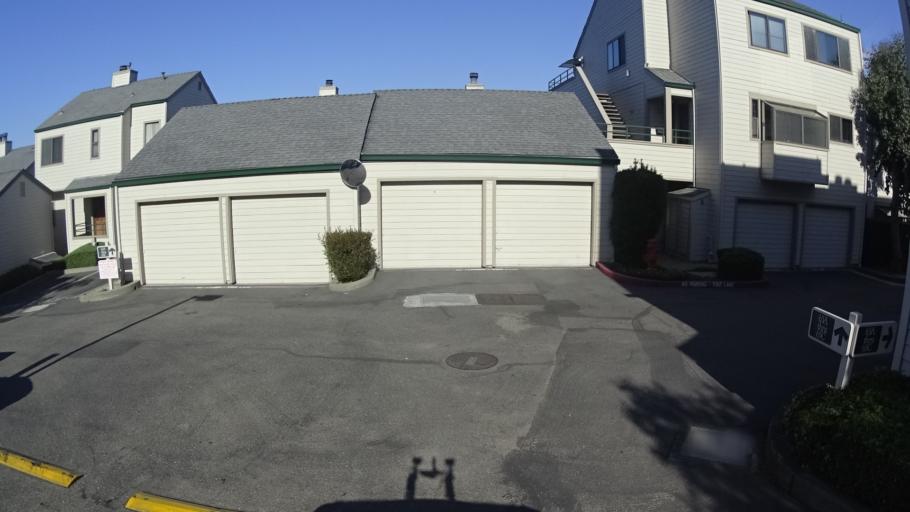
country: US
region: California
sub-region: San Mateo County
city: San Bruno
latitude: 37.6422
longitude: -122.4463
